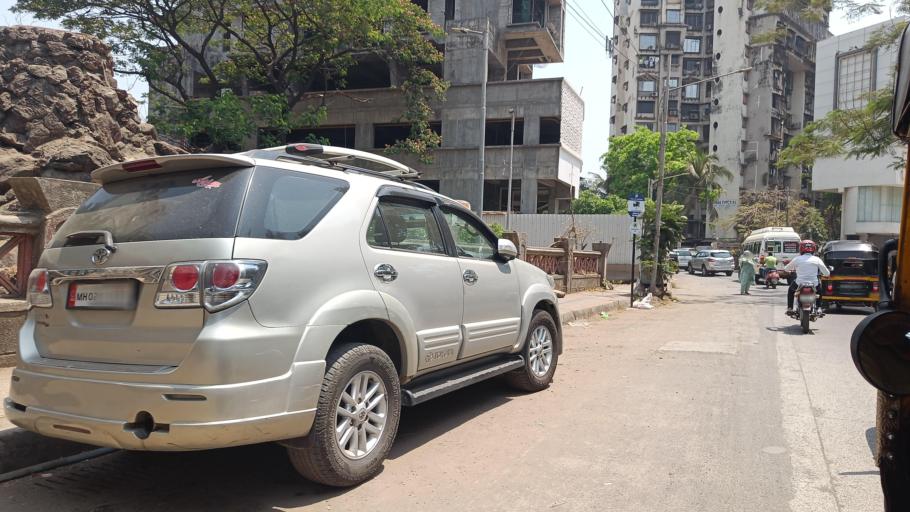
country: IN
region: Maharashtra
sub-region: Mumbai Suburban
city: Powai
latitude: 19.1378
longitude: 72.8413
